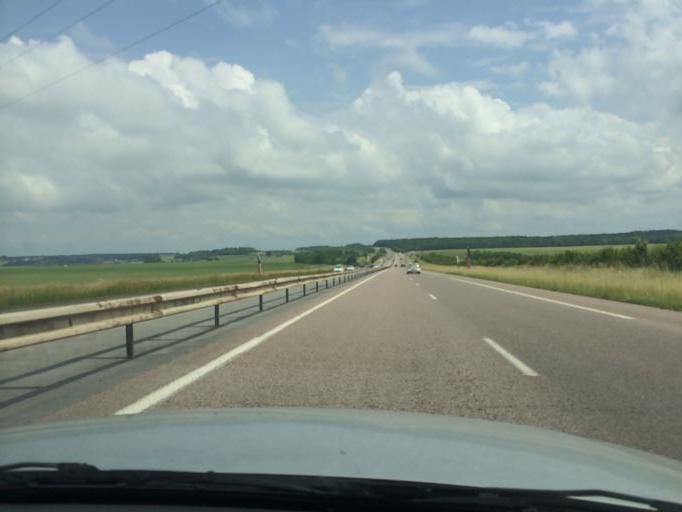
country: FR
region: Picardie
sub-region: Departement de l'Aisne
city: Fere-en-Tardenois
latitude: 49.1282
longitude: 3.5618
